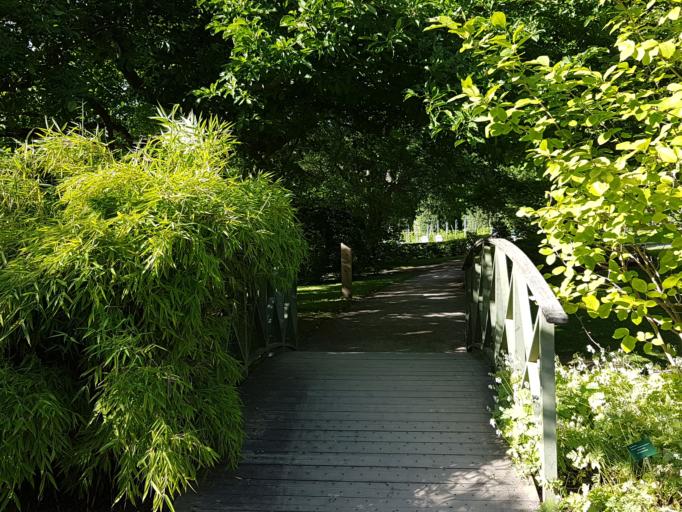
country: SE
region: Gotland
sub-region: Gotland
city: Visby
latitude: 57.6433
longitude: 18.2941
